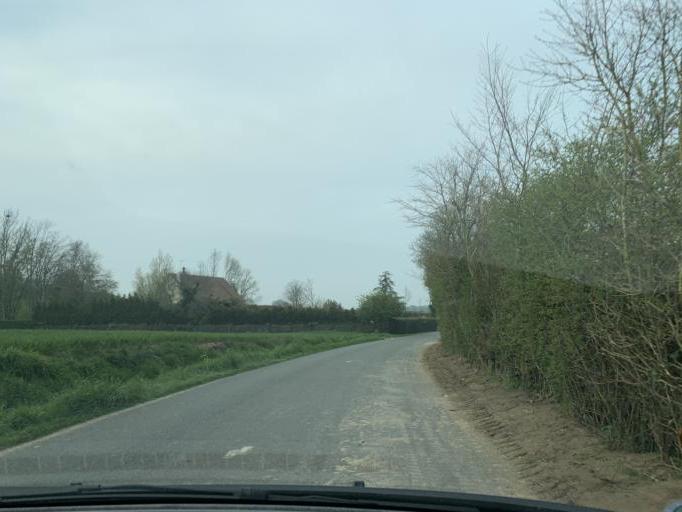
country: FR
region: Nord-Pas-de-Calais
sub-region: Departement du Pas-de-Calais
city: Samer
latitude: 50.6772
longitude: 1.7557
